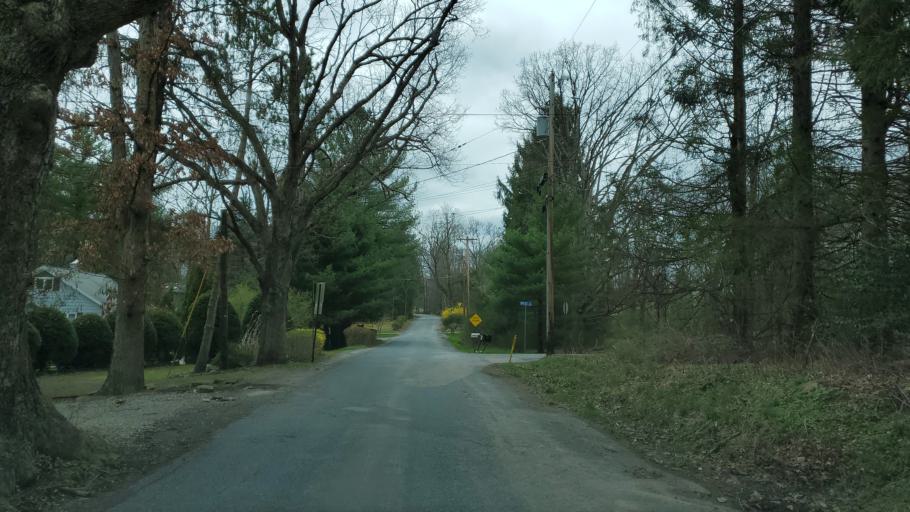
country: US
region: Pennsylvania
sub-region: Westmoreland County
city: Ligonier
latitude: 40.1887
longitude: -79.2440
